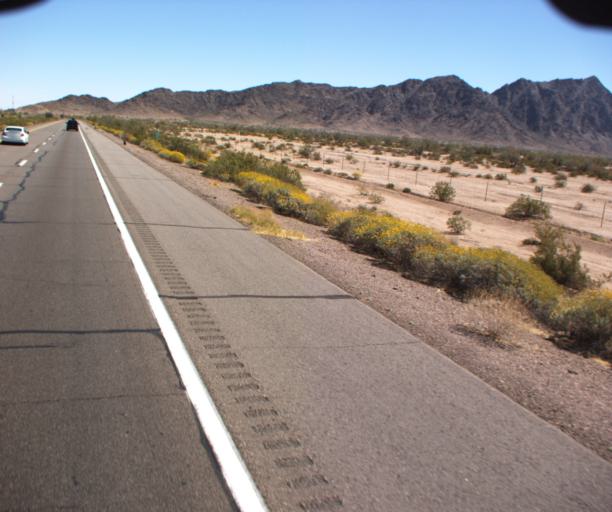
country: US
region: Arizona
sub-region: Yuma County
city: Wellton
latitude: 32.7212
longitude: -113.7696
